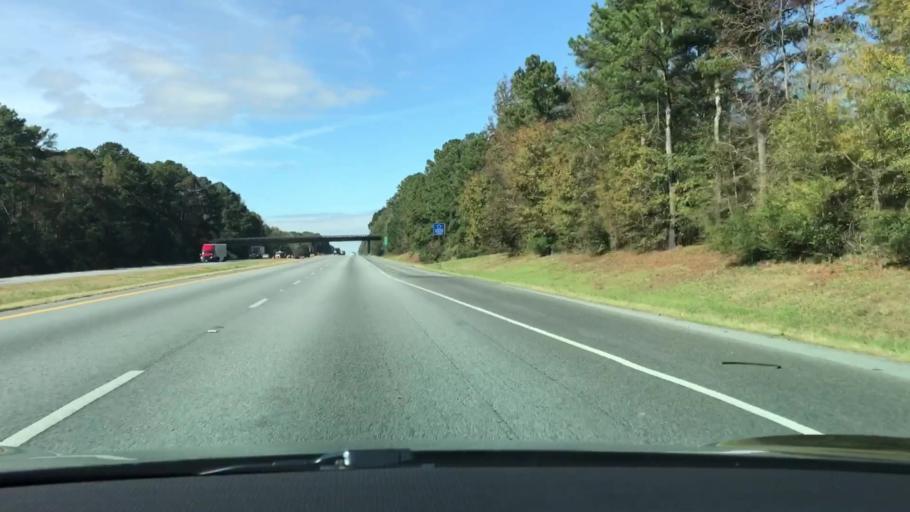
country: US
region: Georgia
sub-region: Morgan County
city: Madison
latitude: 33.5804
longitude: -83.5854
